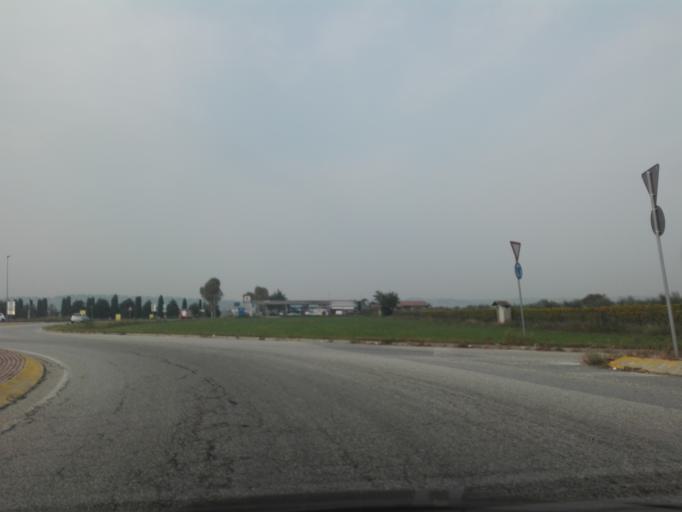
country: IT
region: Veneto
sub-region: Provincia di Verona
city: Lugagnano
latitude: 45.4466
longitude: 10.8643
